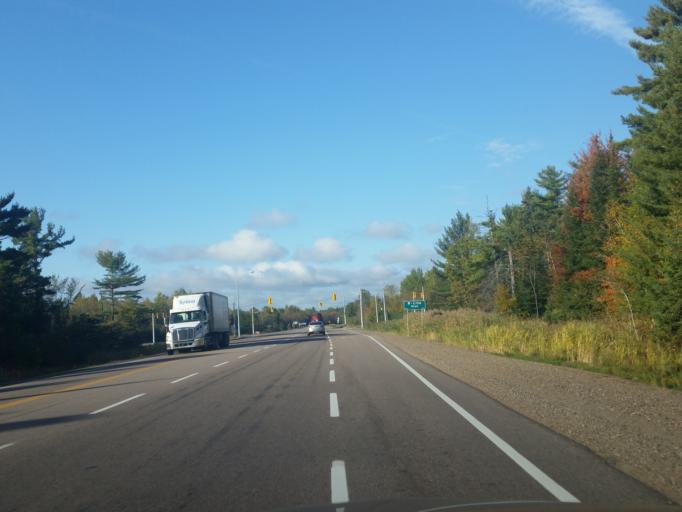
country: CA
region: Ontario
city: Pembroke
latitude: 45.7919
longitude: -77.1653
